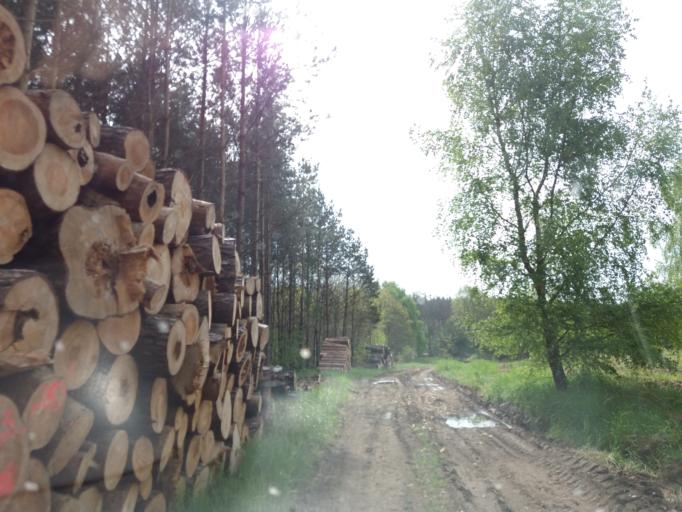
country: PL
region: West Pomeranian Voivodeship
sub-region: Powiat choszczenski
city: Krzecin
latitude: 53.0056
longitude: 15.5495
